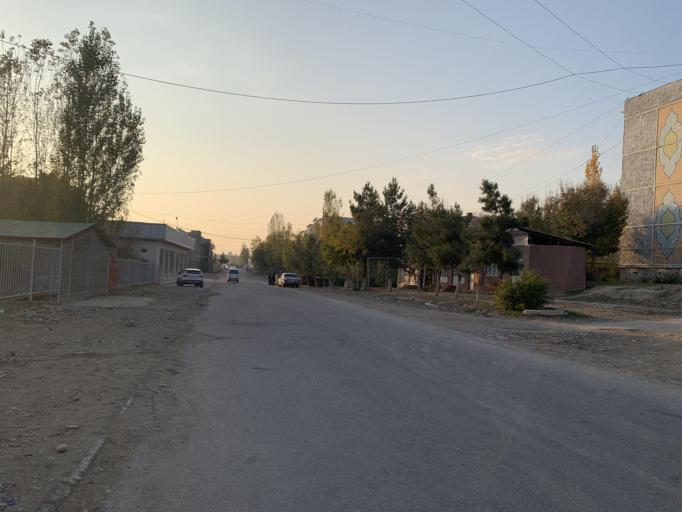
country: UZ
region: Namangan
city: Namangan Shahri
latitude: 41.0026
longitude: 71.6064
